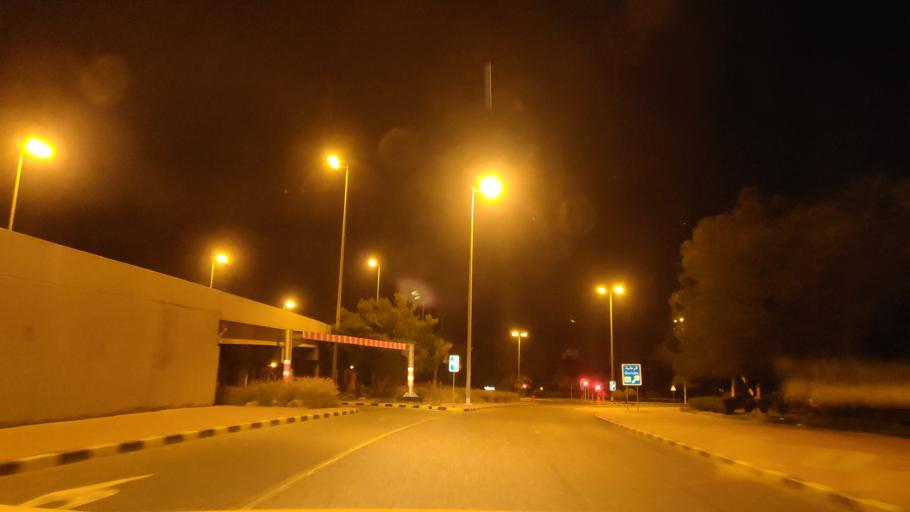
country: KW
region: Al Asimah
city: Ash Shamiyah
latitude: 29.3344
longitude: 47.9862
